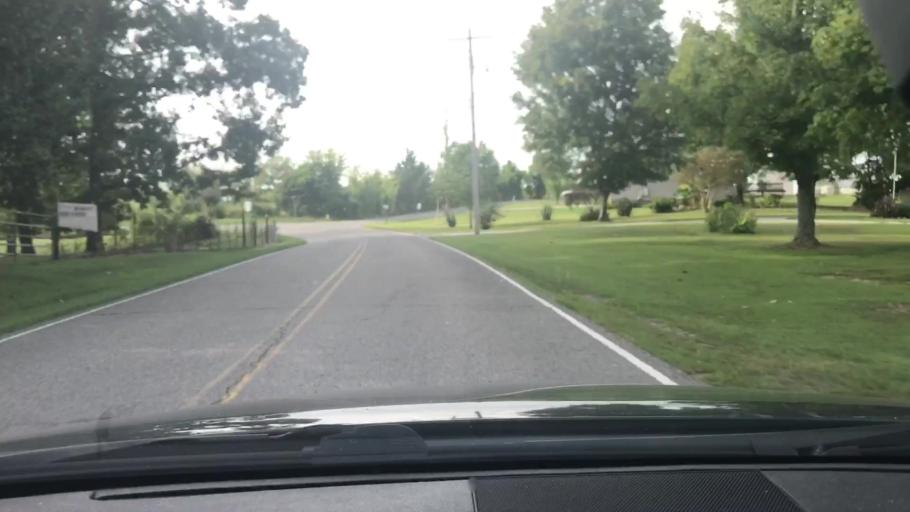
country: US
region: Tennessee
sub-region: Dickson County
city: White Bluff
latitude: 36.1494
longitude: -87.2339
